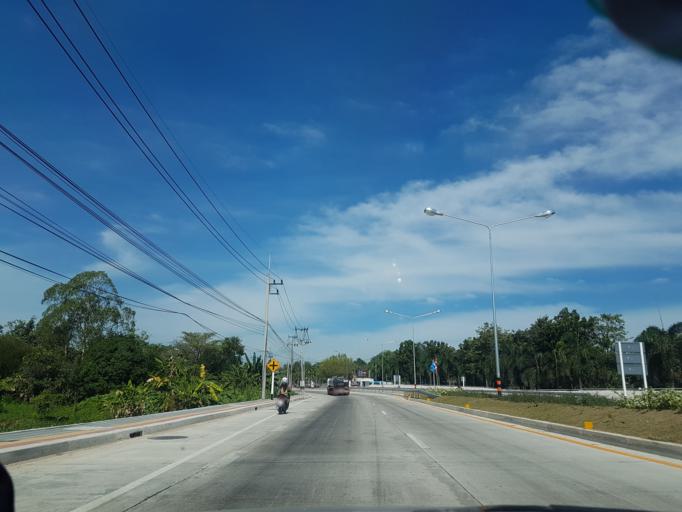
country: TH
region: Chon Buri
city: Sattahip
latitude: 12.6871
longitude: 100.9788
